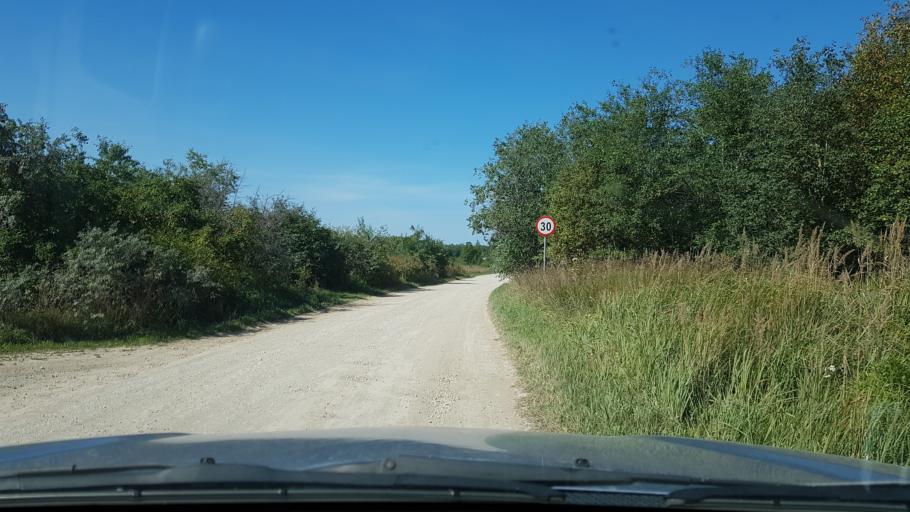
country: EE
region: Ida-Virumaa
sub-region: Sillamaee linn
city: Sillamae
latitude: 59.3726
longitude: 27.7883
